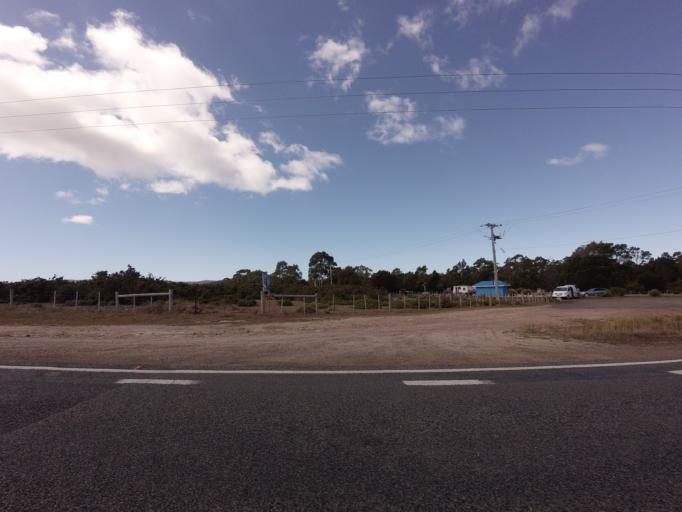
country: AU
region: Tasmania
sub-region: Break O'Day
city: St Helens
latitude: -41.9398
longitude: 148.2203
